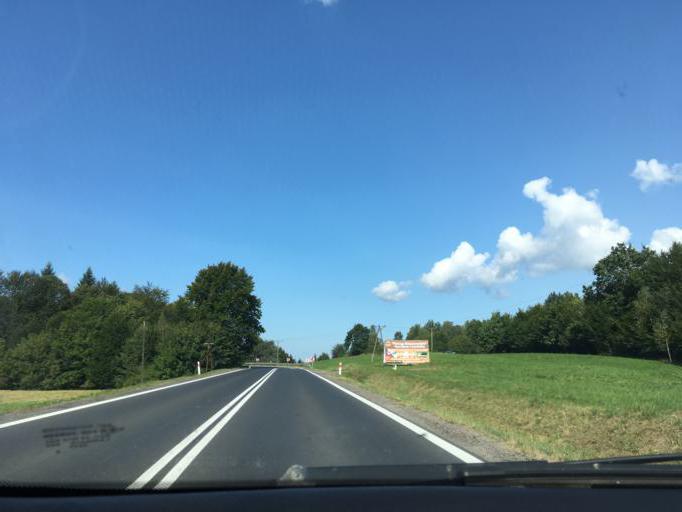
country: PL
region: Subcarpathian Voivodeship
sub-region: Powiat leski
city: Uherce Mineralne
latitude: 49.4680
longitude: 22.3824
